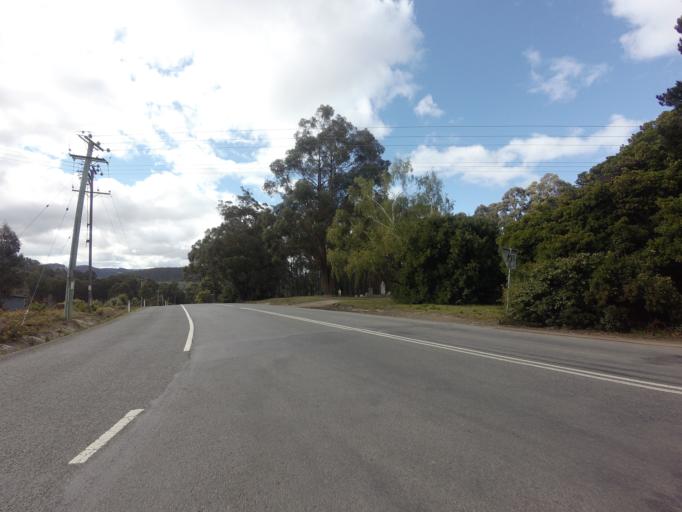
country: AU
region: Tasmania
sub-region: Huon Valley
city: Geeveston
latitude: -43.1973
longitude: 146.9569
